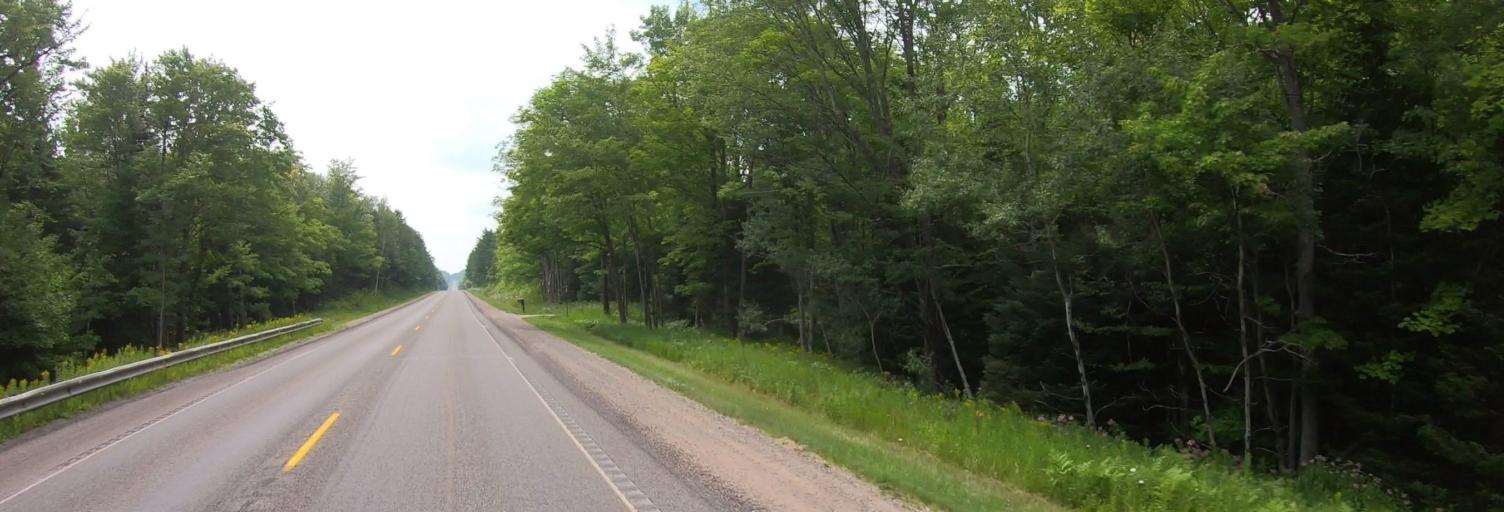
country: US
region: Michigan
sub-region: Alger County
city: Munising
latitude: 46.3705
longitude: -86.7063
